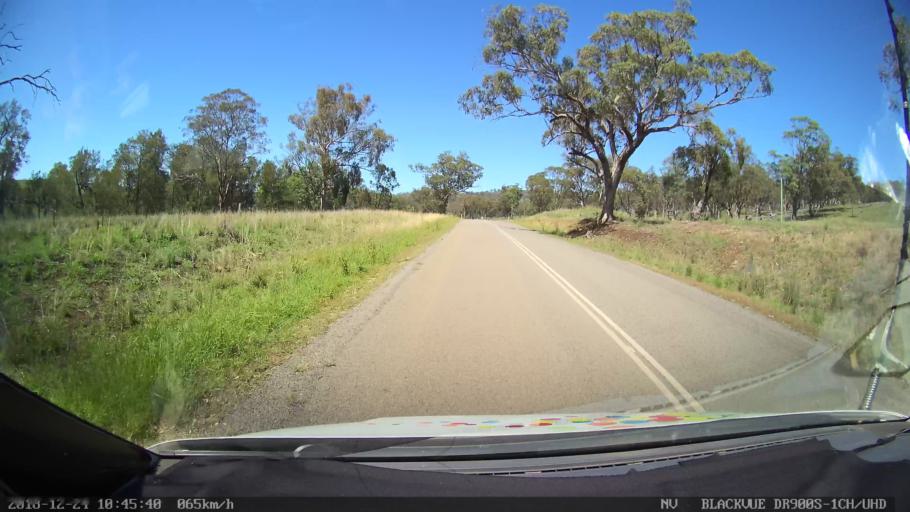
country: AU
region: New South Wales
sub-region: Upper Hunter Shire
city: Merriwa
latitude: -31.9049
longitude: 150.4341
